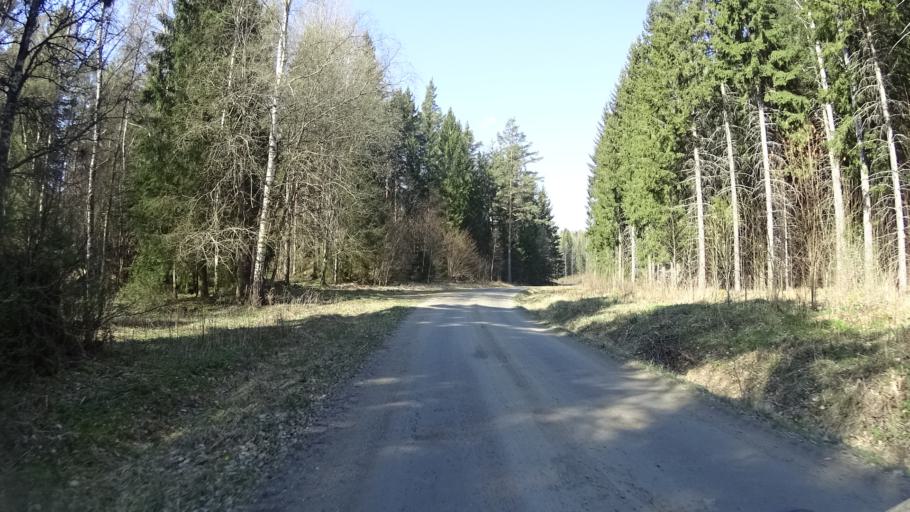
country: SE
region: OEstergoetland
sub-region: Linkopings Kommun
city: Linkoping
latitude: 58.2578
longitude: 15.5752
